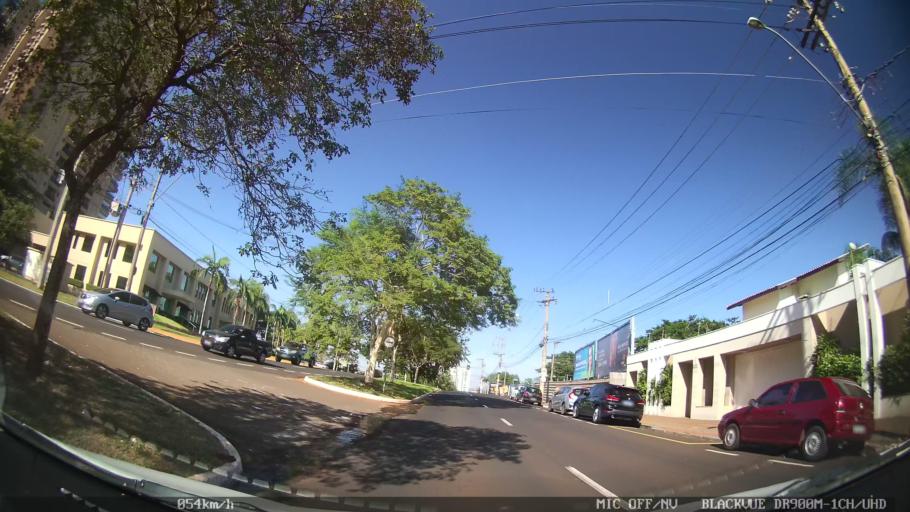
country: BR
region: Sao Paulo
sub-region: Ribeirao Preto
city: Ribeirao Preto
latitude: -21.2184
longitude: -47.8057
